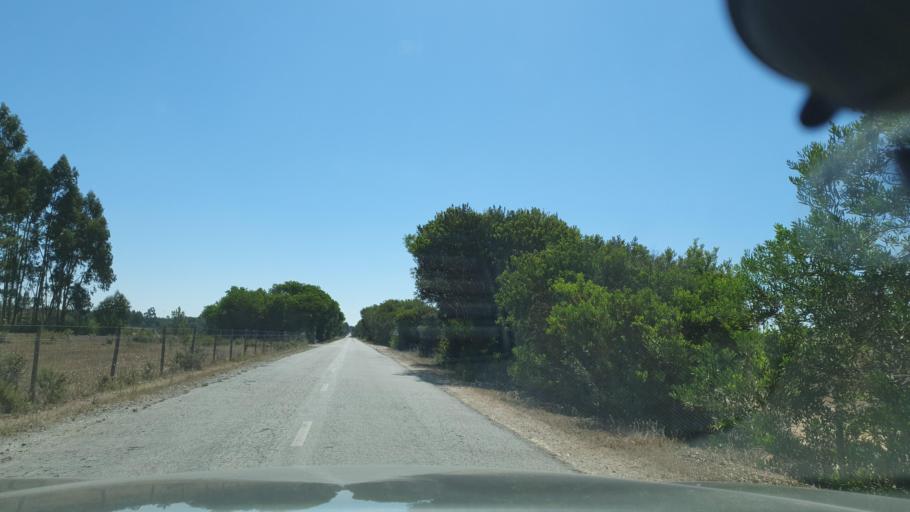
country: PT
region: Beja
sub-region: Odemira
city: Sao Teotonio
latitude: 37.5008
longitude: -8.6818
